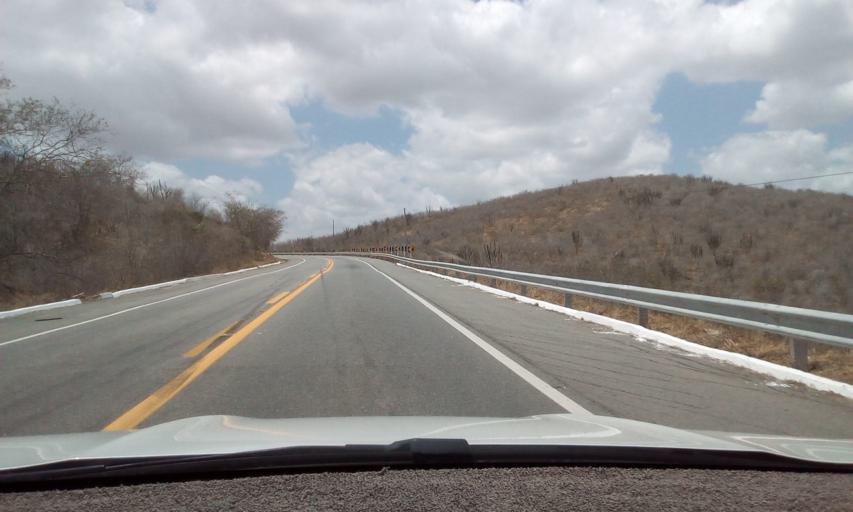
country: BR
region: Paraiba
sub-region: Boqueirao
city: Boqueirao
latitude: -7.6679
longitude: -36.0808
